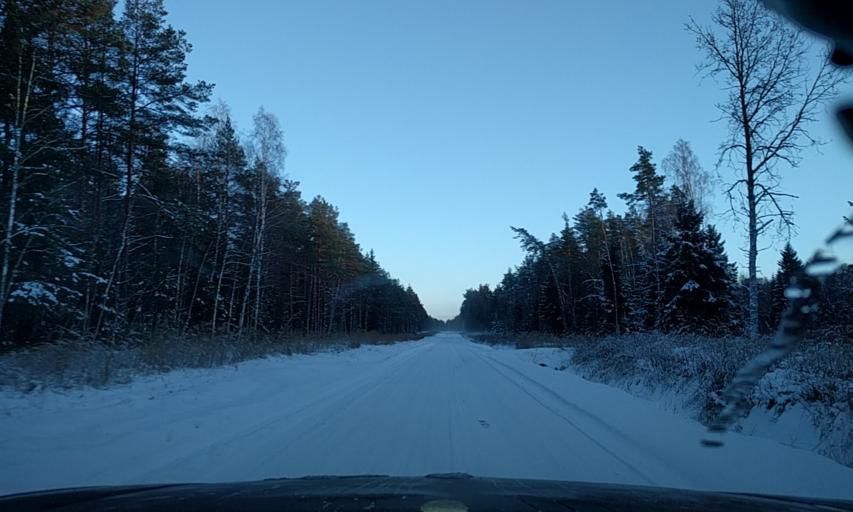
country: EE
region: Harju
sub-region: Saku vald
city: Saku
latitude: 59.3219
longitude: 24.6639
